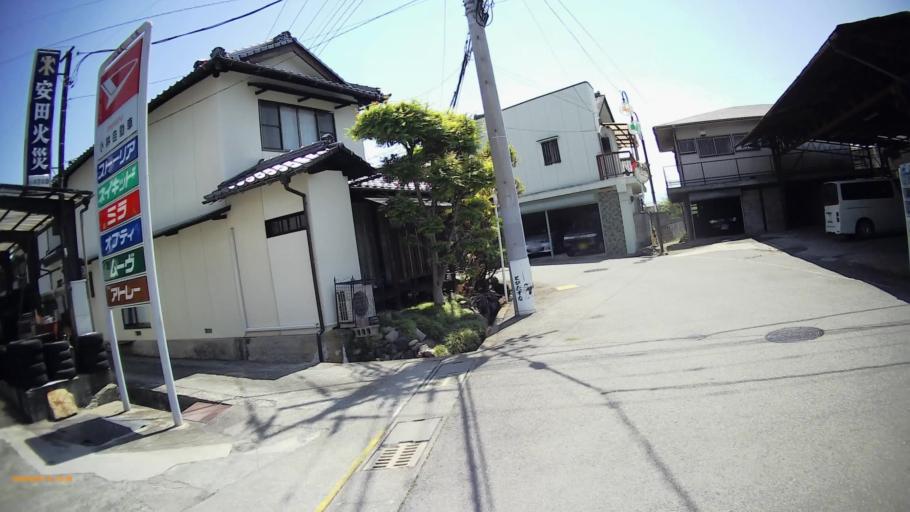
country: JP
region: Yamanashi
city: Nirasaki
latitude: 35.6954
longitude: 138.4723
